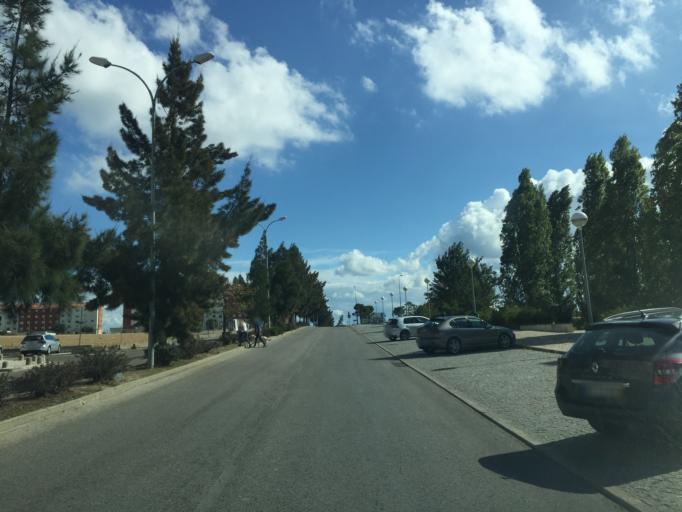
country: PT
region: Lisbon
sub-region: Odivelas
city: Olival do Basto
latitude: 38.7784
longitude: -9.1489
